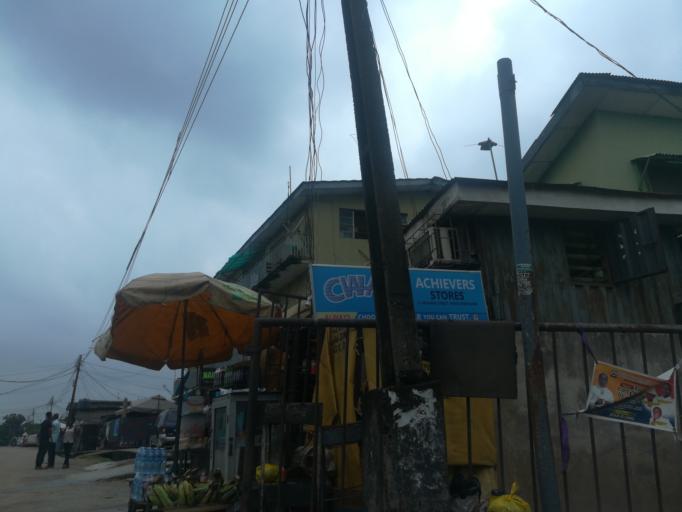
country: NG
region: Lagos
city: Ojota
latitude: 6.5711
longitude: 3.3736
